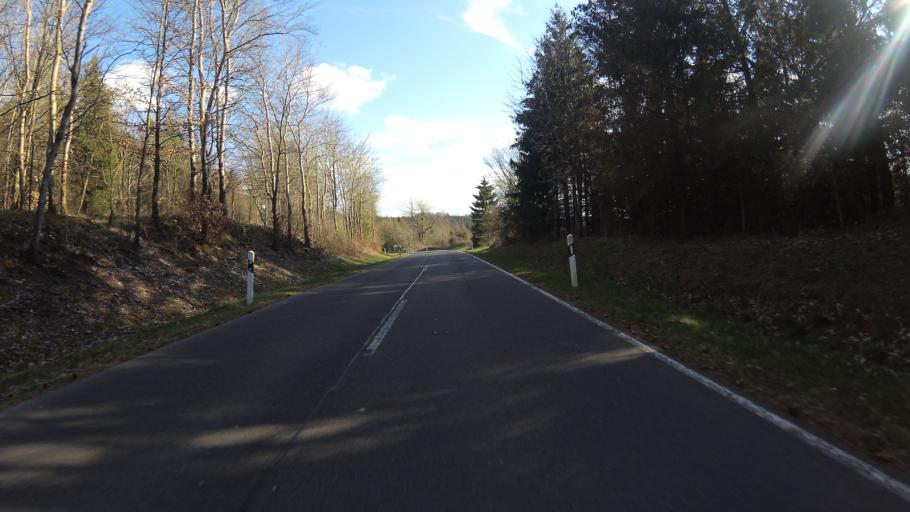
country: DE
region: Rheinland-Pfalz
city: Nurburg
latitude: 50.3284
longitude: 6.9452
